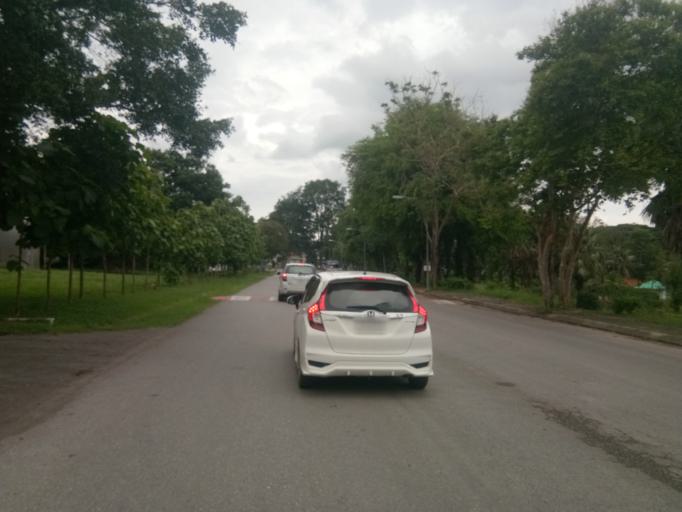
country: TH
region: Chiang Rai
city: Chiang Rai
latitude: 19.9829
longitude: 99.8501
